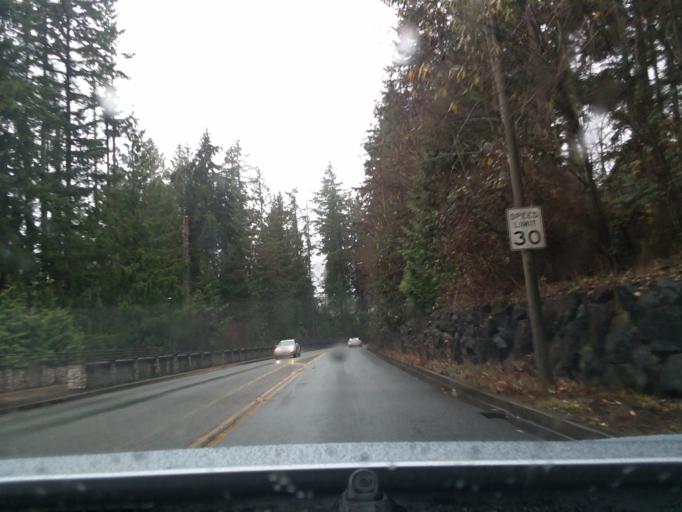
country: US
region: Washington
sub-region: Snohomish County
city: Mill Creek
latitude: 47.8765
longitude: -122.2184
